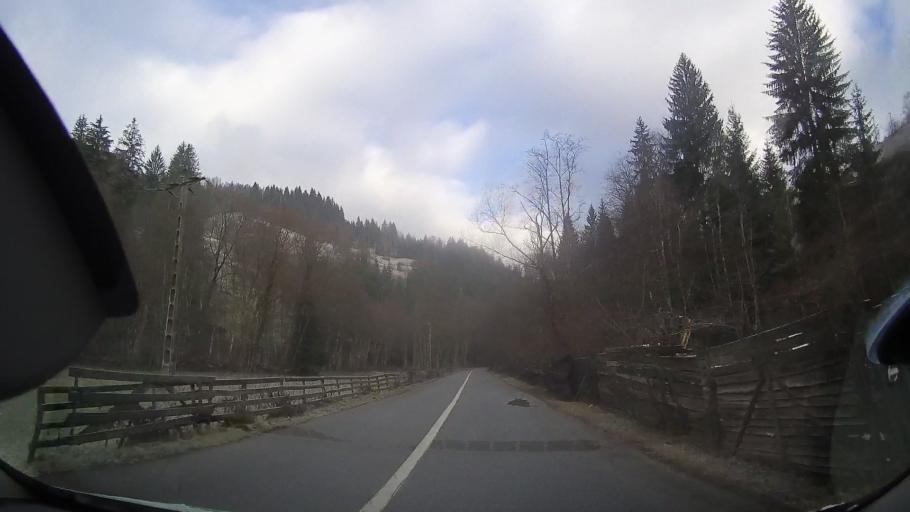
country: RO
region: Alba
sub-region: Comuna Horea
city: Horea
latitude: 46.4805
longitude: 22.9615
